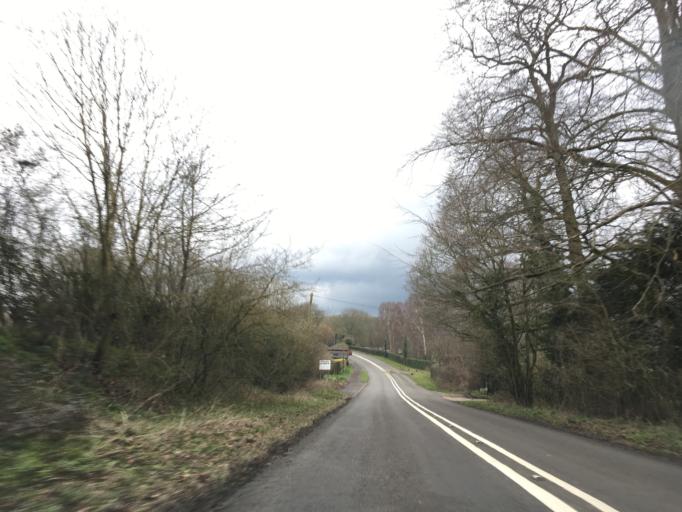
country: GB
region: England
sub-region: Hampshire
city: Colden Common
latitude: 51.0053
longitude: -1.3202
